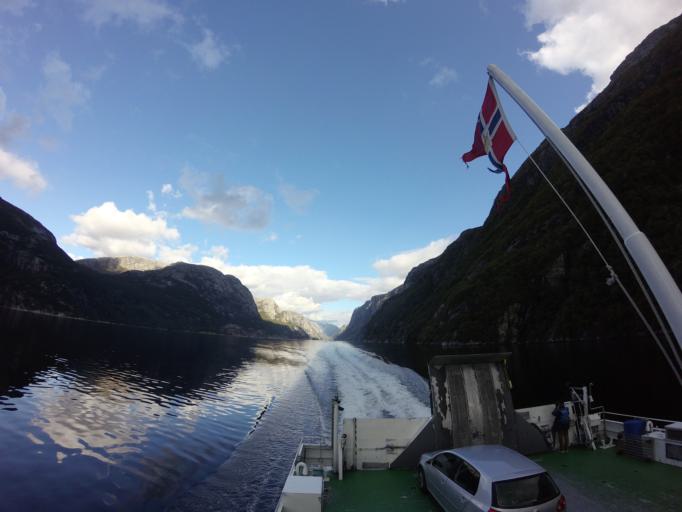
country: NO
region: Rogaland
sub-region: Hjelmeland
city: Hjelmelandsvagen
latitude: 59.0262
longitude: 6.4805
